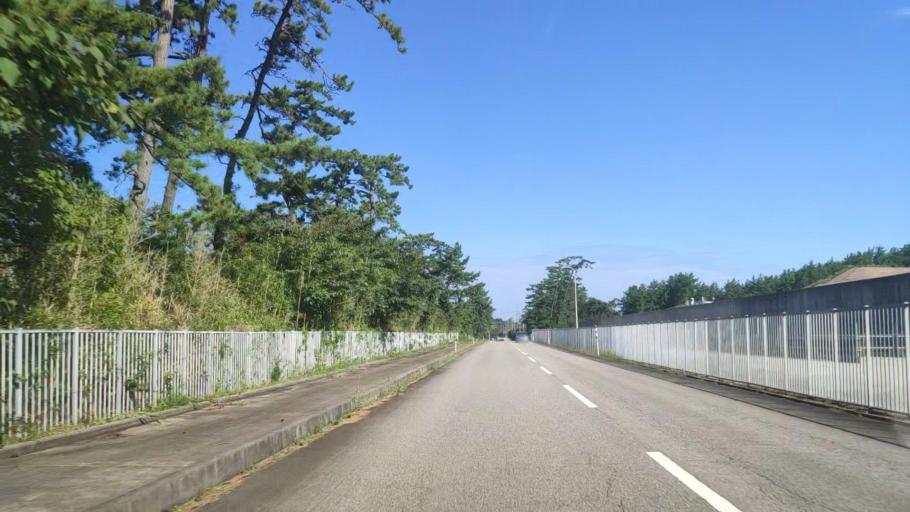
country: JP
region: Ishikawa
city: Hakui
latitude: 37.0615
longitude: 136.7234
